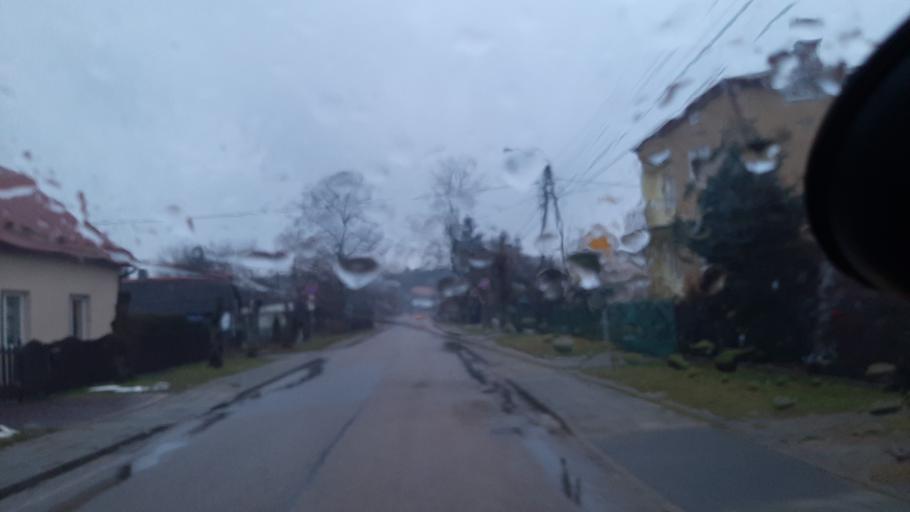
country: PL
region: Lublin Voivodeship
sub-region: Powiat lubartowski
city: Firlej
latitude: 51.5565
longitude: 22.5083
